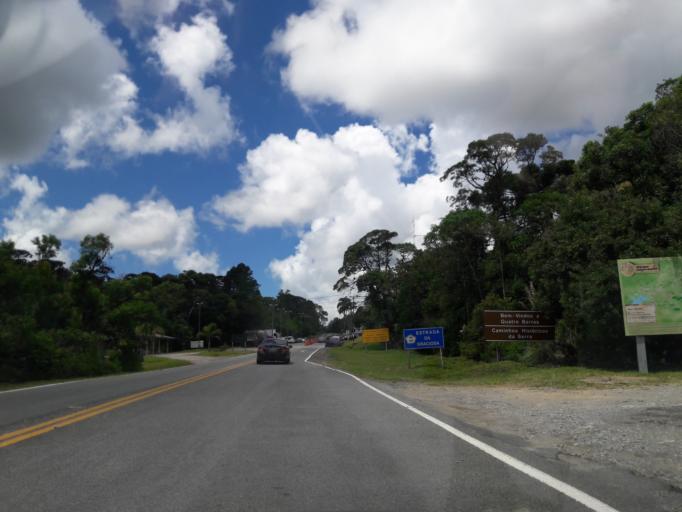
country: BR
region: Parana
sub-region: Campina Grande Do Sul
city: Campina Grande do Sul
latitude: -25.3063
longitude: -48.9450
